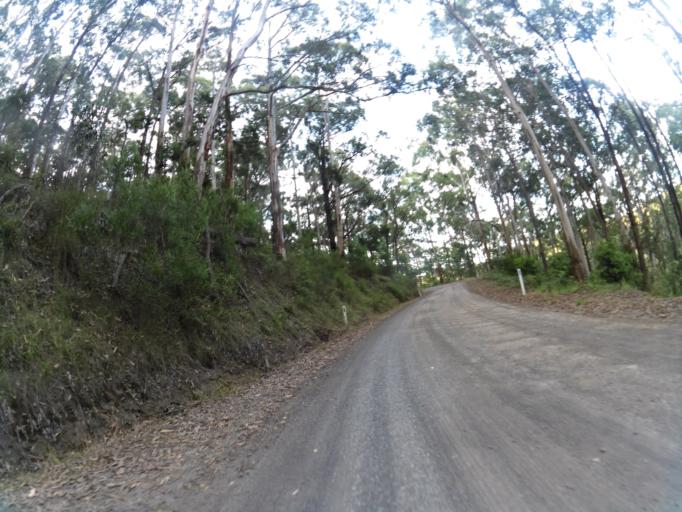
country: AU
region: Victoria
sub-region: Colac-Otway
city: Apollo Bay
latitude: -38.5469
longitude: 143.7336
